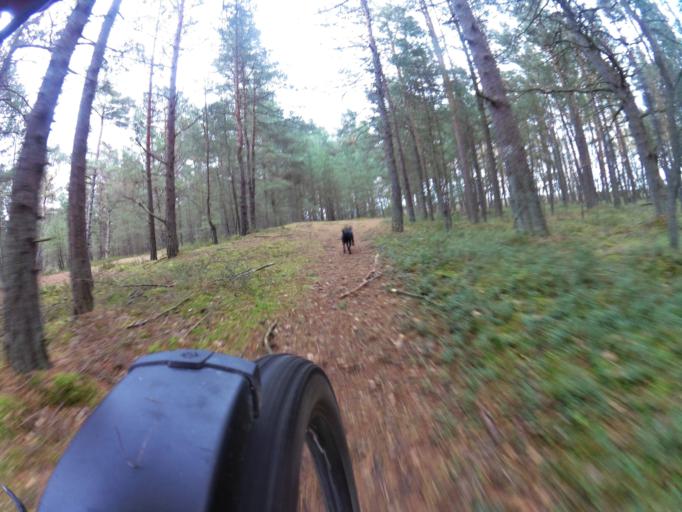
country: PL
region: Pomeranian Voivodeship
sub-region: Powiat leborski
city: Leba
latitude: 54.7736
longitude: 17.6462
